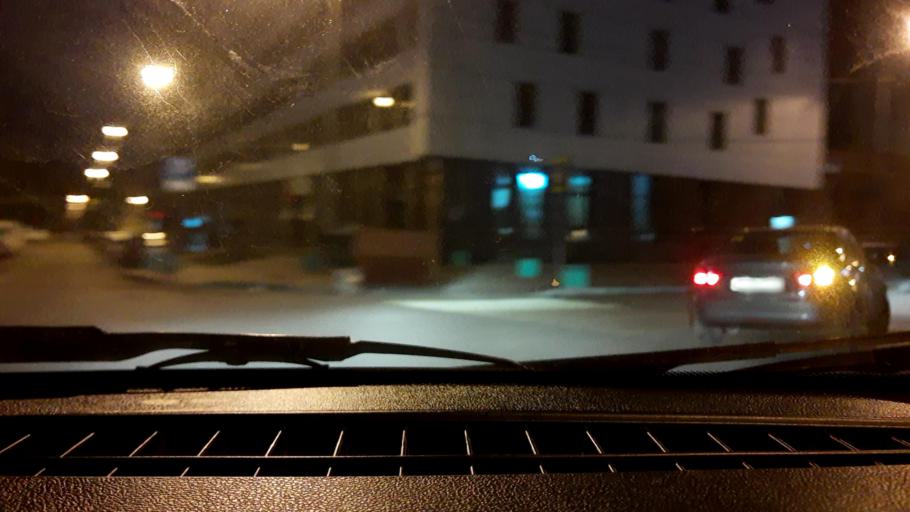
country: RU
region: Bashkortostan
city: Ufa
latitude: 54.7821
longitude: 56.0295
